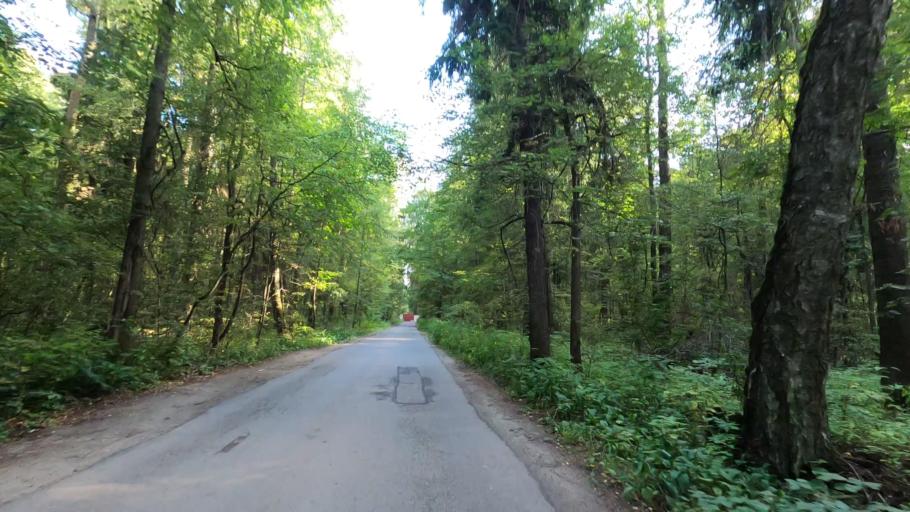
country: RU
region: Moskovskaya
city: Raduzhnyy
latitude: 55.1773
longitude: 38.7431
